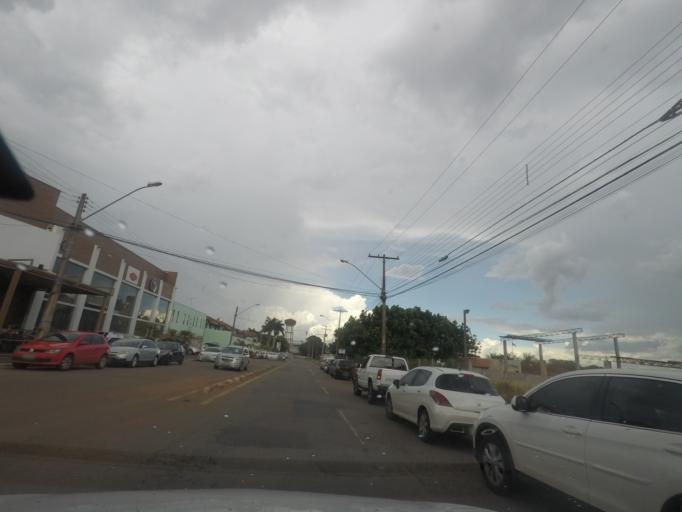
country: BR
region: Goias
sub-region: Goiania
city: Goiania
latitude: -16.6360
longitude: -49.2269
